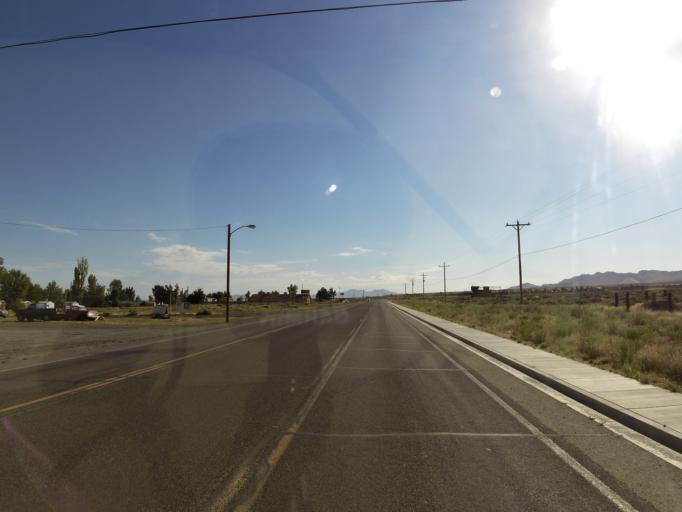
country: US
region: Nevada
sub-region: Humboldt County
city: Winnemucca
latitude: 40.9793
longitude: -117.7097
